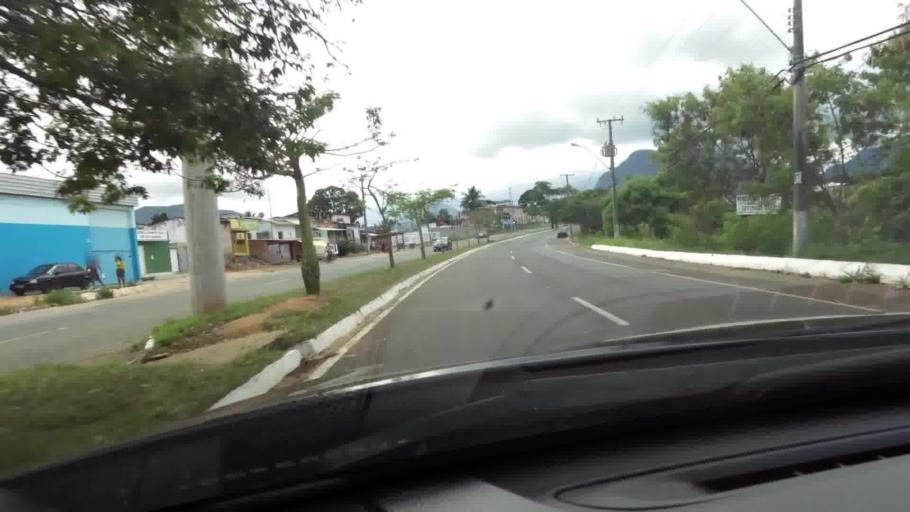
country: BR
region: Espirito Santo
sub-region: Guarapari
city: Guarapari
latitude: -20.6435
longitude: -40.5169
